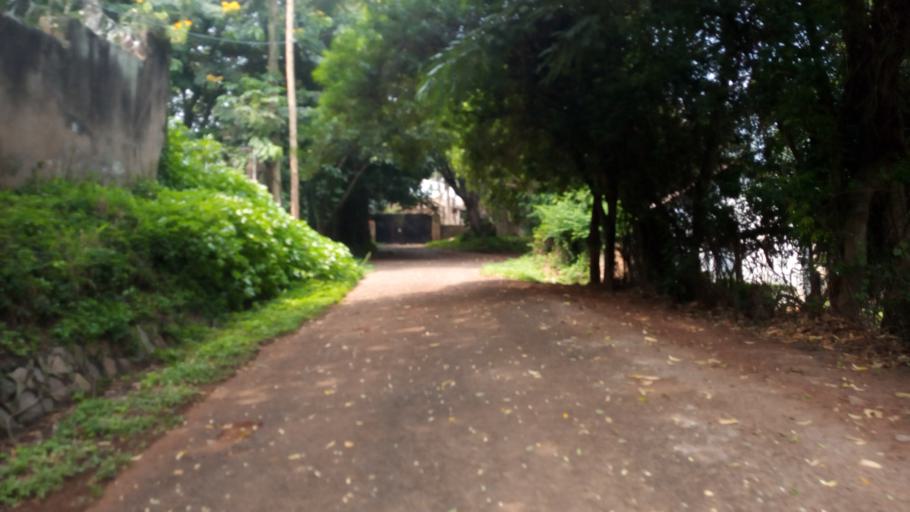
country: UG
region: Central Region
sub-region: Wakiso District
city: Kireka
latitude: 0.3232
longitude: 32.6262
